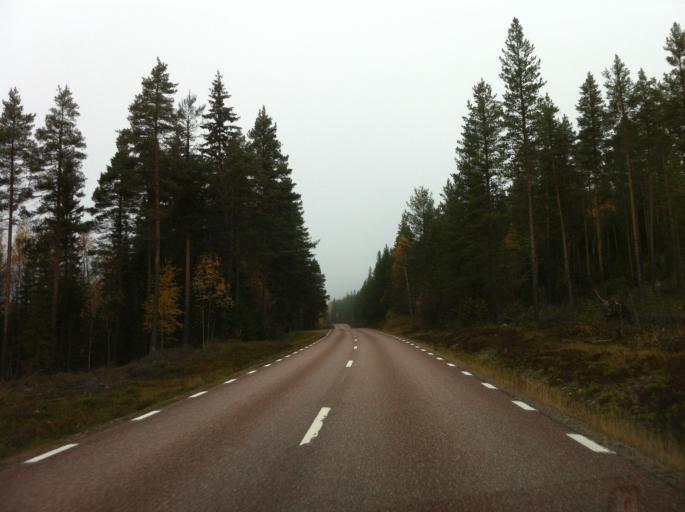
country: NO
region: Hedmark
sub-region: Trysil
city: Innbygda
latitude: 61.7798
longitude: 12.9412
